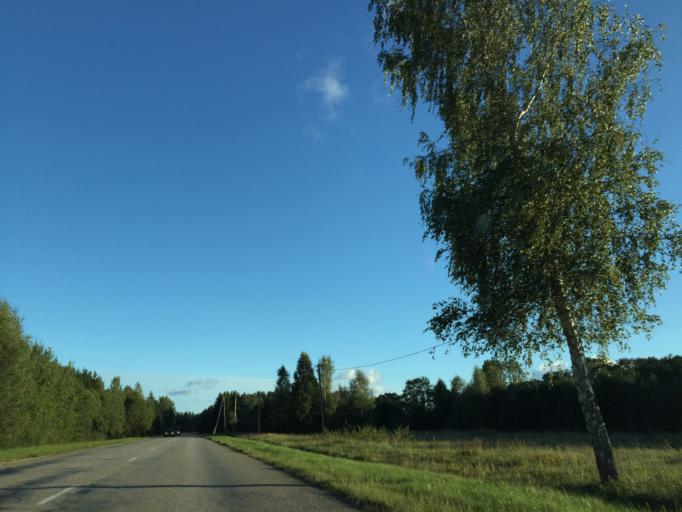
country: LV
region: Kuldigas Rajons
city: Kuldiga
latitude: 56.9191
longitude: 22.0539
